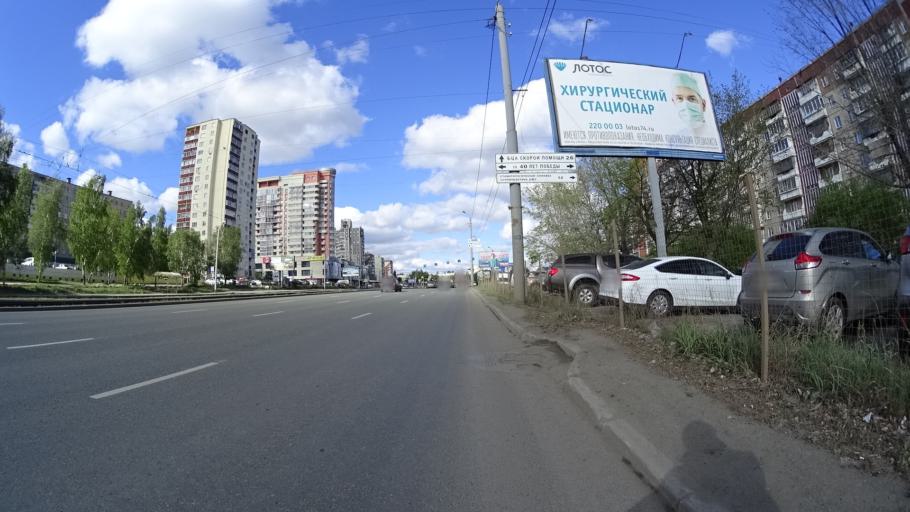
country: RU
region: Chelyabinsk
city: Roshchino
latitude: 55.1847
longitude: 61.2973
